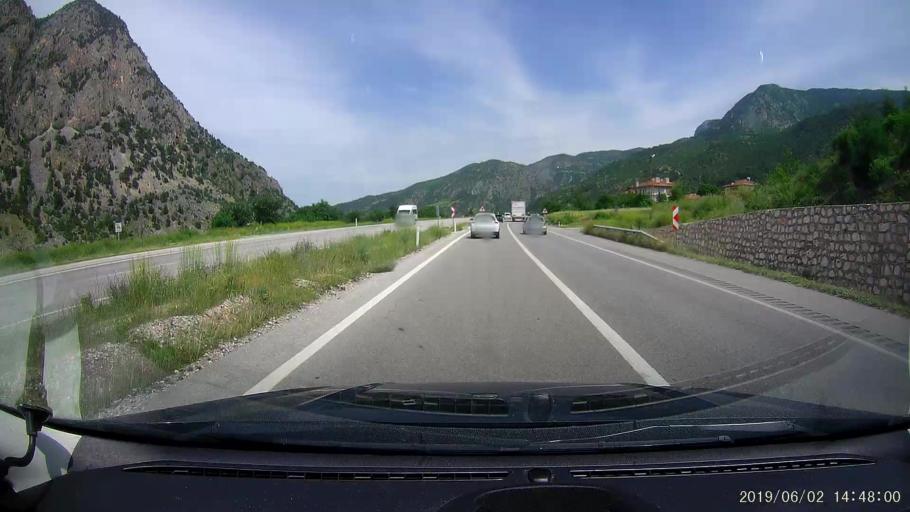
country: TR
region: Corum
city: Hacihamza
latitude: 41.0652
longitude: 34.4715
